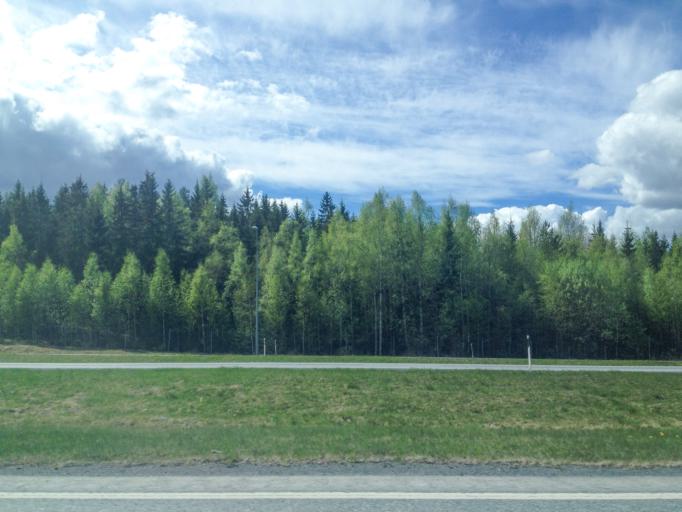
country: FI
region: Pirkanmaa
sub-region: Etelae-Pirkanmaa
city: Viiala
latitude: 61.2580
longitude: 23.8347
